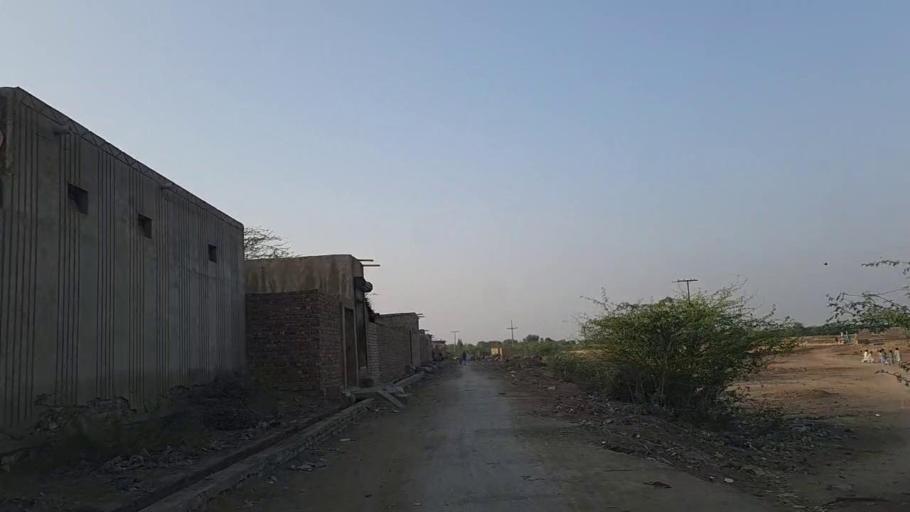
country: PK
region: Sindh
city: Pithoro
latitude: 25.5072
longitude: 69.3887
